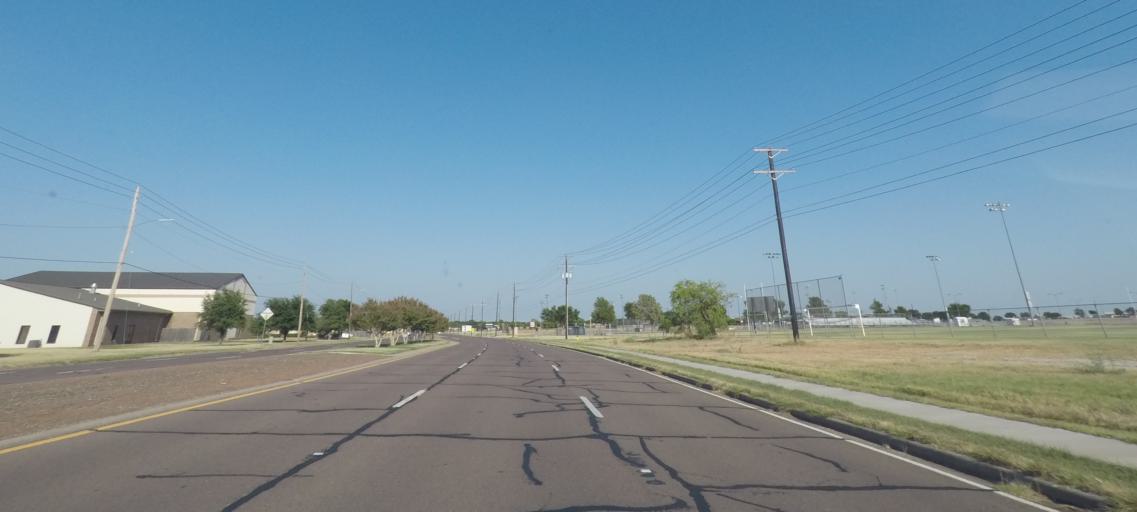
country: US
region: Texas
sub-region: Wichita County
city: Wichita Falls
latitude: 33.8582
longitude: -98.5844
